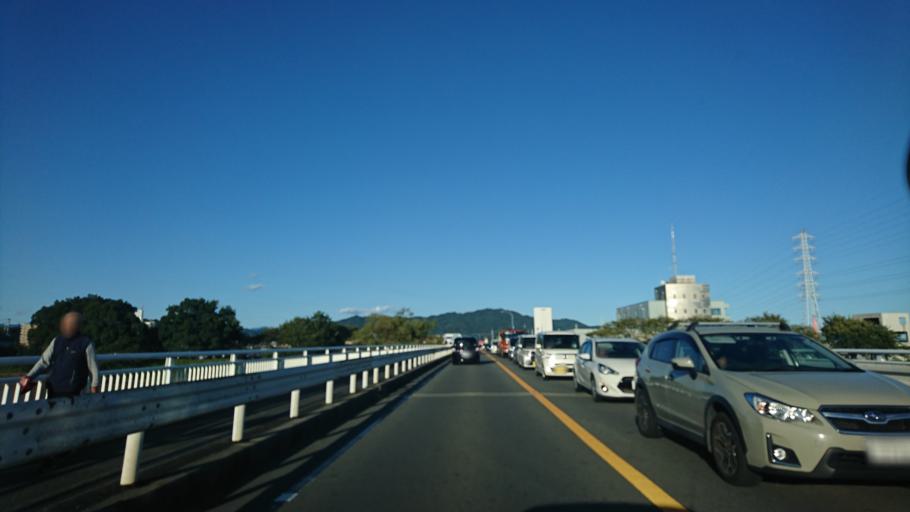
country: JP
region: Shizuoka
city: Fujieda
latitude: 34.8628
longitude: 138.2539
